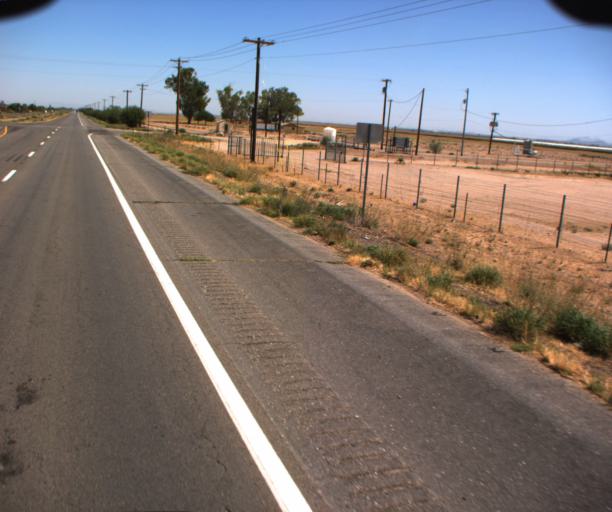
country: US
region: Arizona
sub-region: Pinal County
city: Maricopa
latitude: 32.8929
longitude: -112.0493
